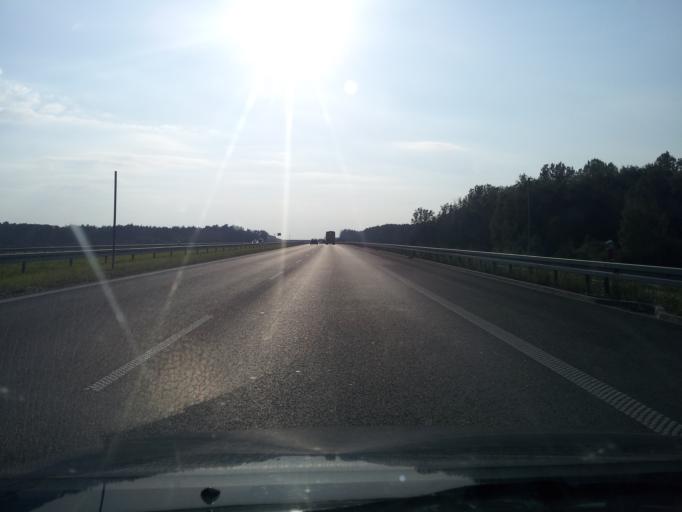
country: PL
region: Lodz Voivodeship
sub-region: Powiat skierniewicki
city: Bolimow
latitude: 52.0731
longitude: 20.2085
